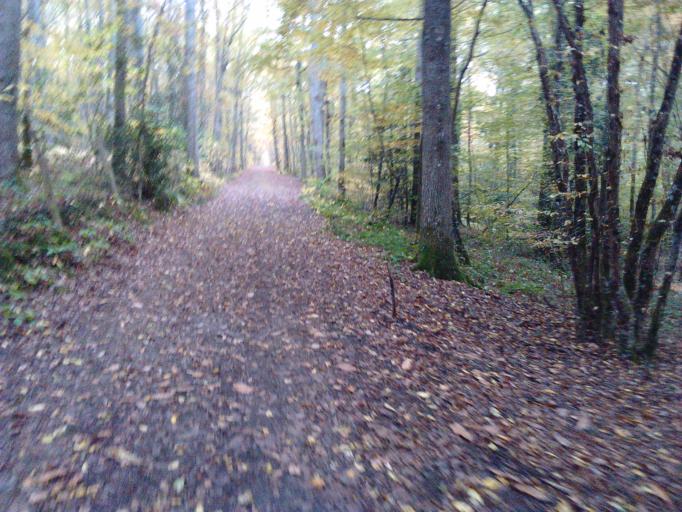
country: FR
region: Centre
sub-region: Departement du Loir-et-Cher
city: Naveil
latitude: 47.8173
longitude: 1.0403
